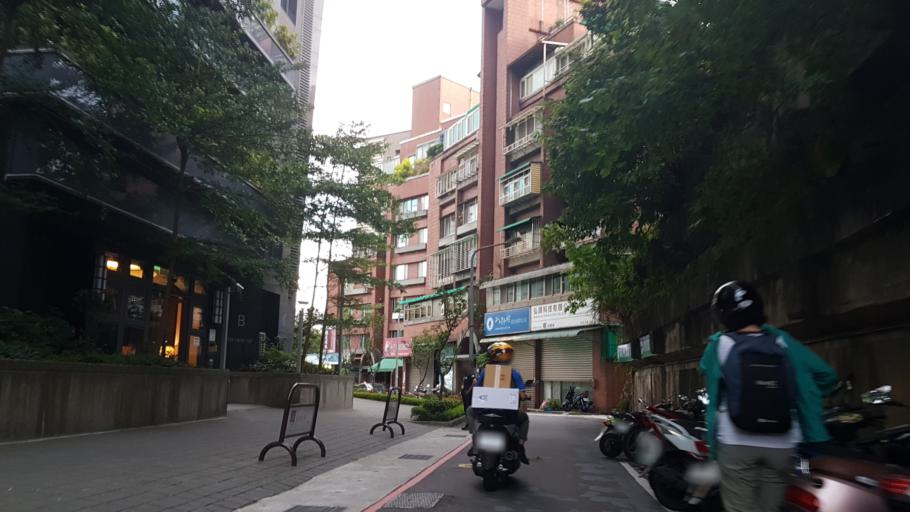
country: TW
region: Taipei
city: Taipei
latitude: 25.0053
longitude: 121.5565
